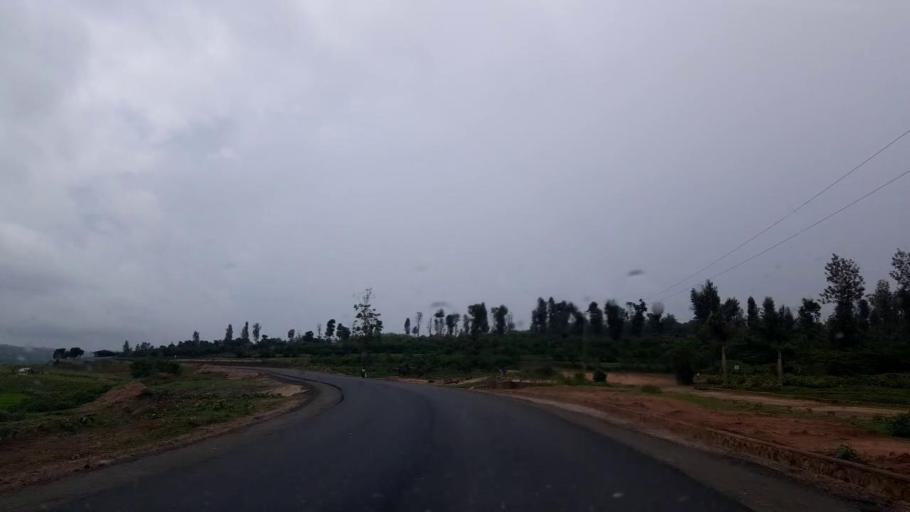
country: RW
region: Northern Province
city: Byumba
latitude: -1.4100
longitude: 30.2851
